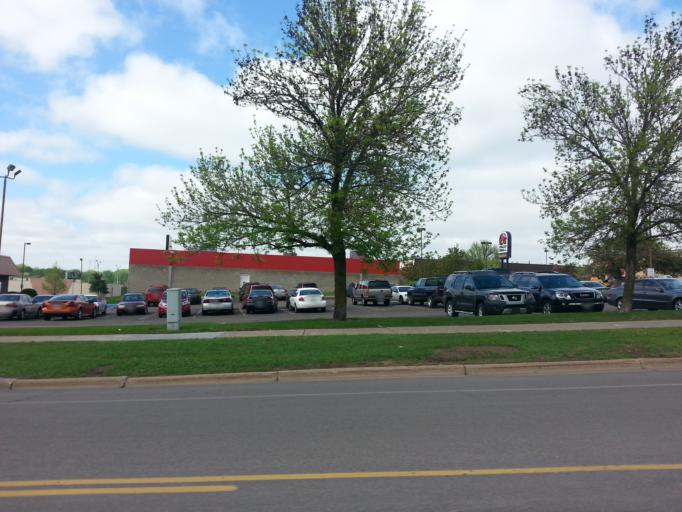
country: US
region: Minnesota
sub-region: Ramsey County
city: Maplewood
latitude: 44.9487
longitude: -93.0191
